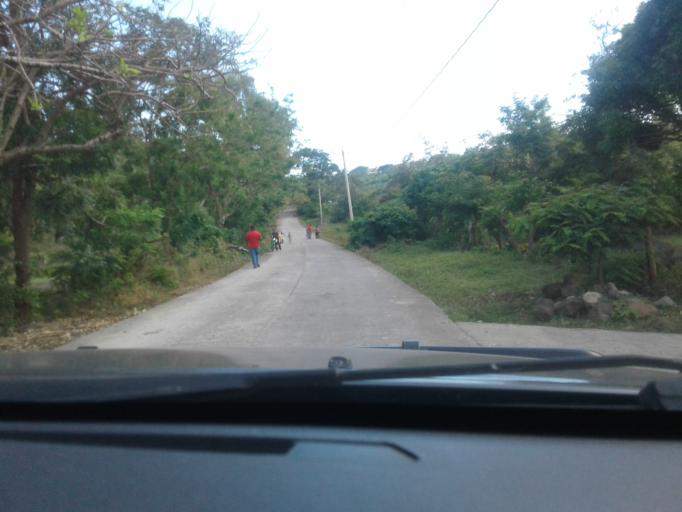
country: NI
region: Rivas
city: Altagracia
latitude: 11.4779
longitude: -85.4693
